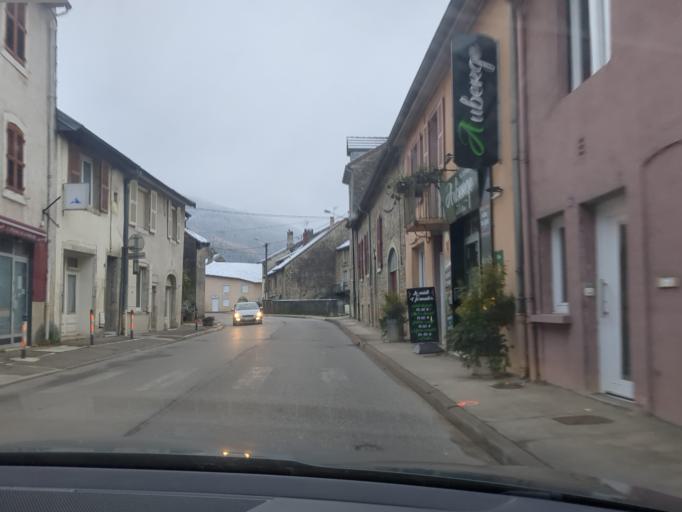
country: FR
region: Franche-Comte
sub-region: Departement du Jura
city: Perrigny
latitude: 46.6540
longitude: 5.5990
